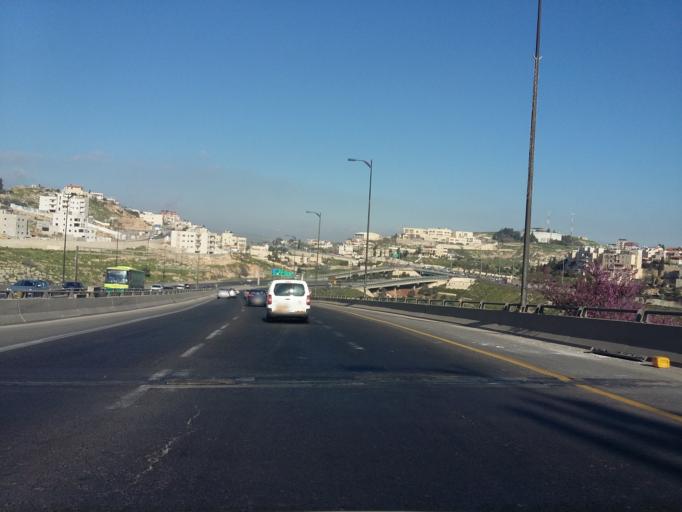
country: PS
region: West Bank
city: `Anata
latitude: 31.8156
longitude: 35.2373
